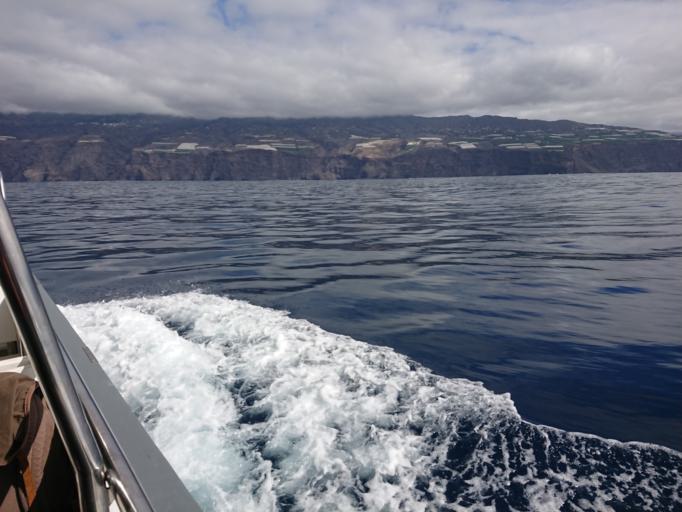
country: ES
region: Canary Islands
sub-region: Provincia de Santa Cruz de Tenerife
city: Tijarafe
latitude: 28.6707
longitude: -18.0056
